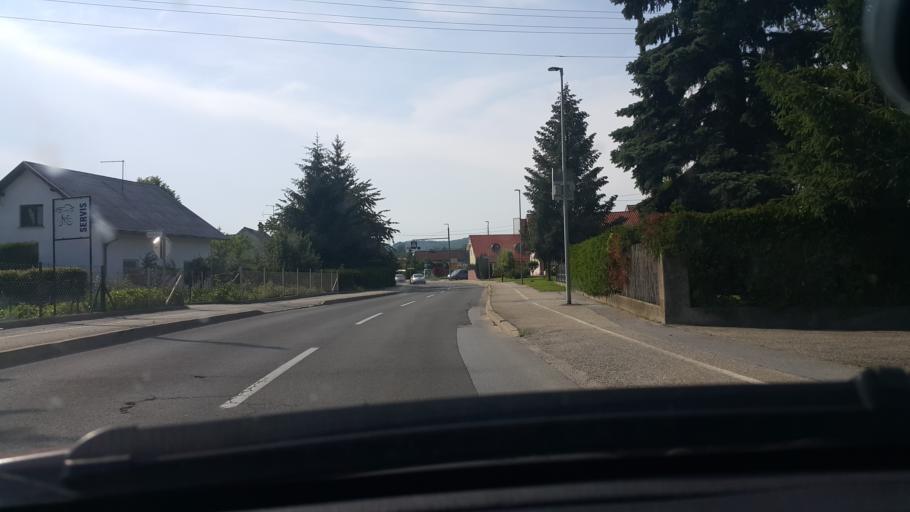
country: SI
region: Duplek
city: Spodnji Duplek
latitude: 46.5040
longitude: 15.7435
